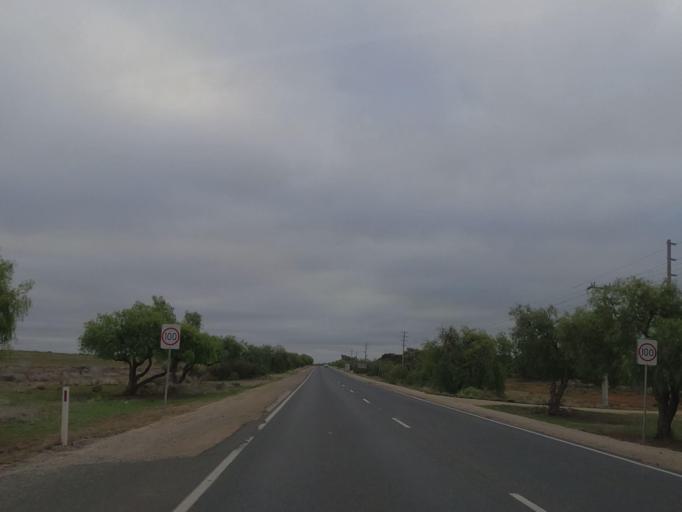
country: AU
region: Victoria
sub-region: Swan Hill
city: Swan Hill
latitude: -35.4493
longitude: 143.6231
